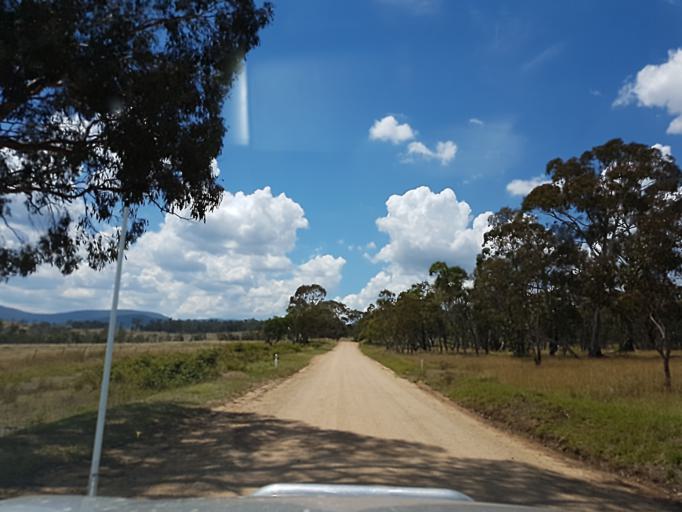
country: AU
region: Victoria
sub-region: Alpine
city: Mount Beauty
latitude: -36.8987
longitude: 147.8420
